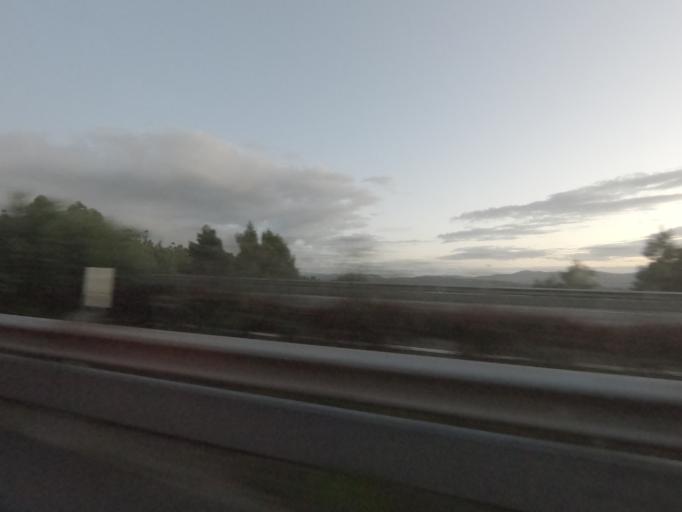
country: PT
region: Porto
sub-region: Paredes
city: Recarei
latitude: 41.1649
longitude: -8.3974
